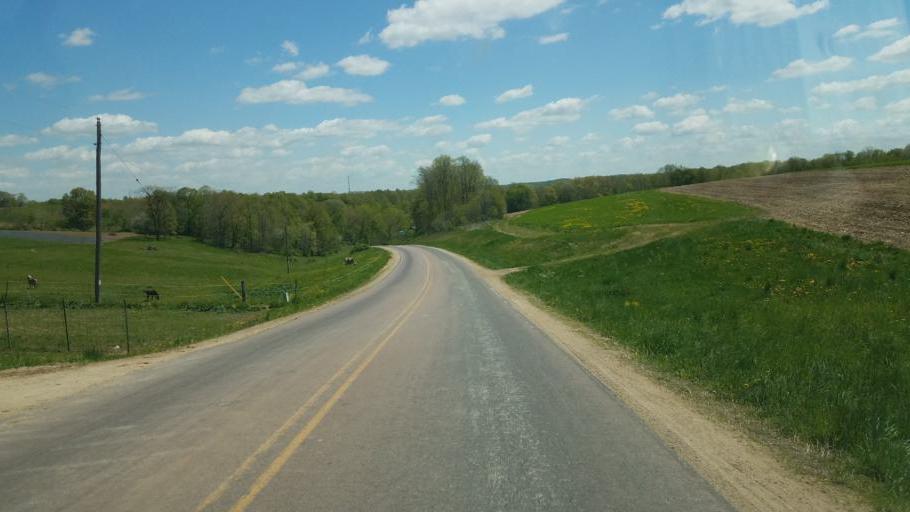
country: US
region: Wisconsin
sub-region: Vernon County
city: Hillsboro
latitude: 43.6462
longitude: -90.4461
